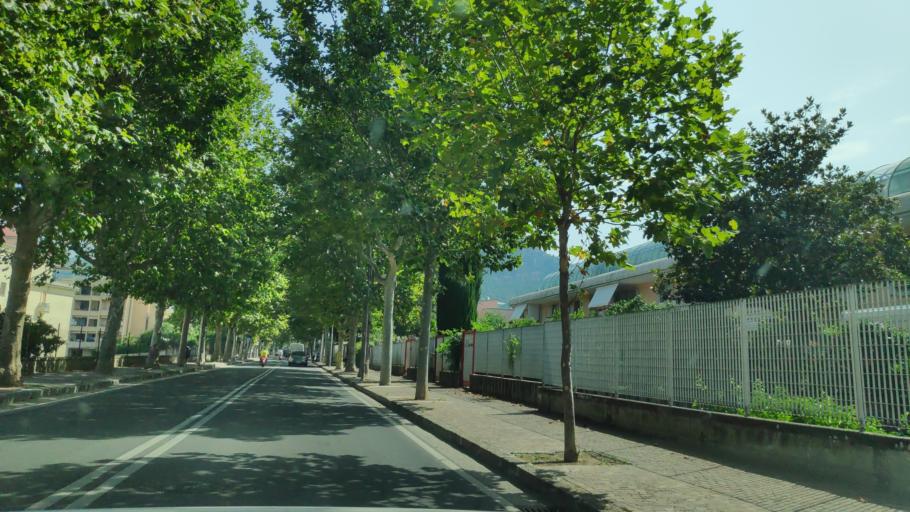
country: IT
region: Campania
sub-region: Provincia di Napoli
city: Piano di Sorrento
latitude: 40.6304
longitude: 14.4142
